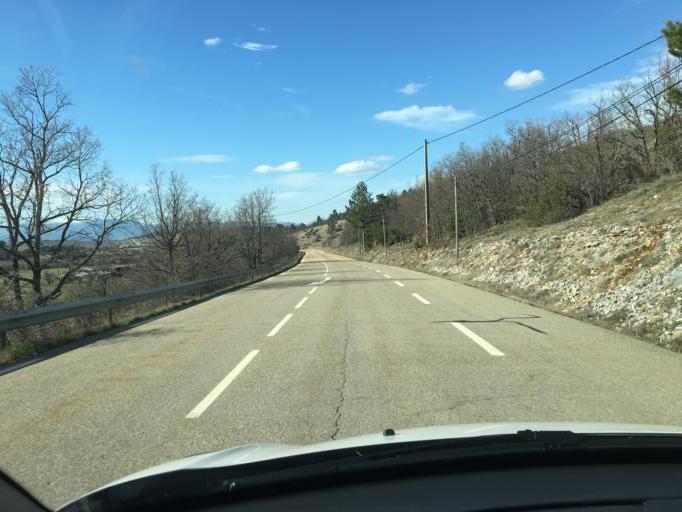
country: FR
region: Provence-Alpes-Cote d'Azur
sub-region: Departement du Vaucluse
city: Sault
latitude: 44.0119
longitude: 5.4755
